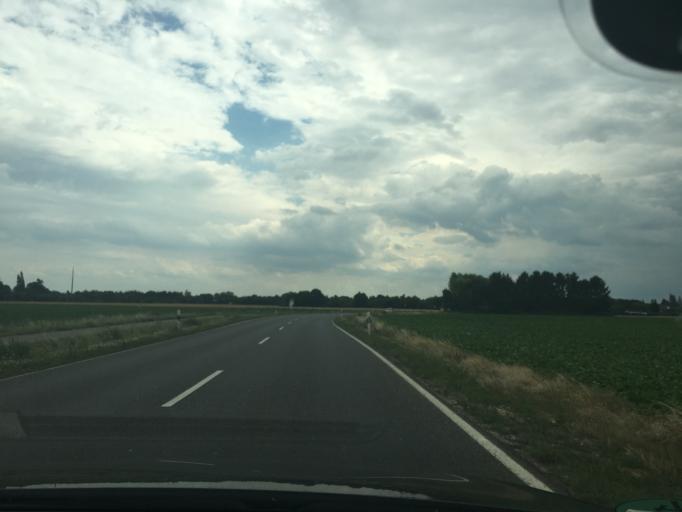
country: DE
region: North Rhine-Westphalia
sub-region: Regierungsbezirk Koln
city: Dueren
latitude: 50.8256
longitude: 6.4915
